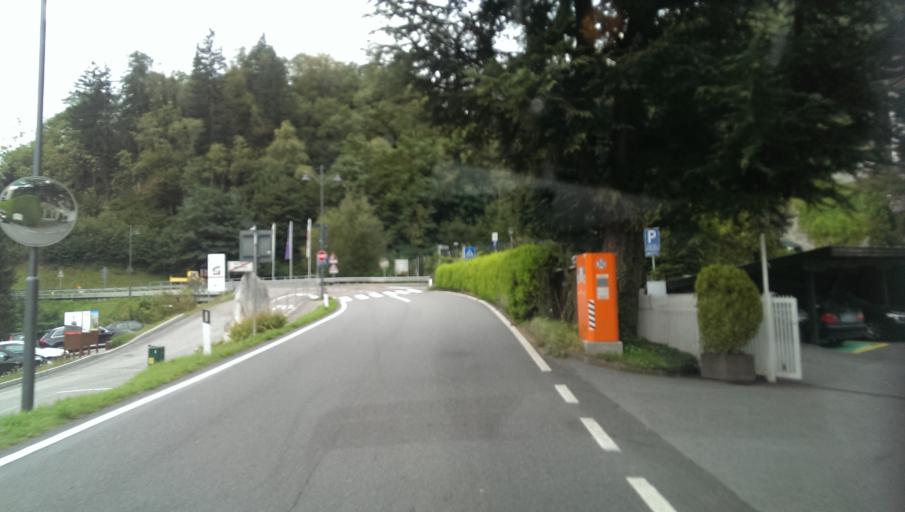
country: IT
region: Trentino-Alto Adige
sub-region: Bolzano
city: Rifiano
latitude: 46.7290
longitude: 11.1999
